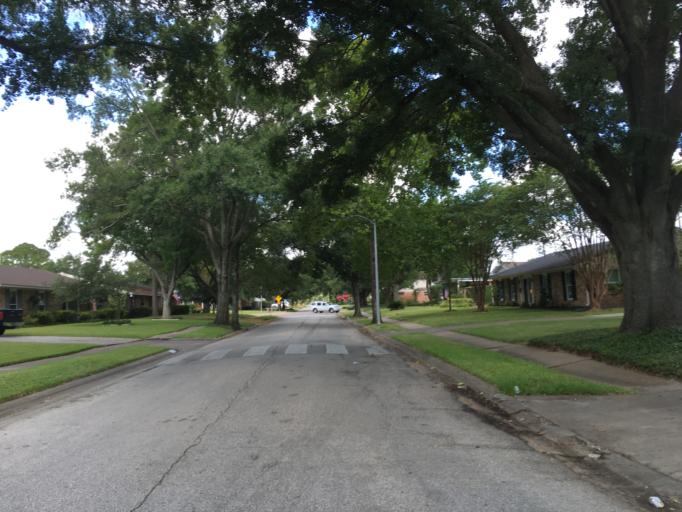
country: US
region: Texas
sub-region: Harris County
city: Piney Point Village
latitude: 29.7346
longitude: -95.5048
